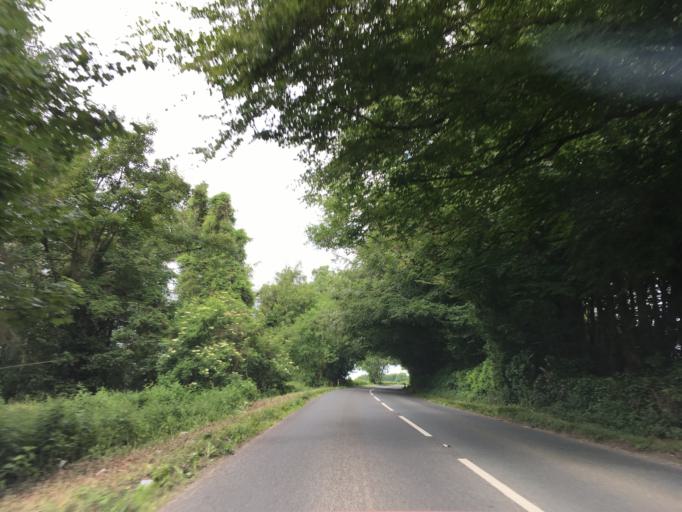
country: GB
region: England
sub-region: Gloucestershire
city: Nailsworth
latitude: 51.6557
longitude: -2.2497
